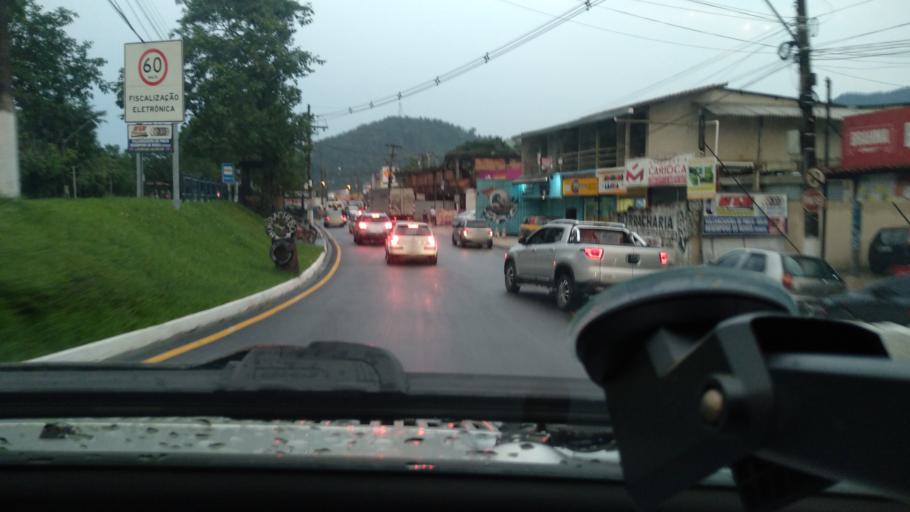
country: BR
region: Rio de Janeiro
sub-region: Angra Dos Reis
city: Angra dos Reis
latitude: -23.0195
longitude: -44.5330
